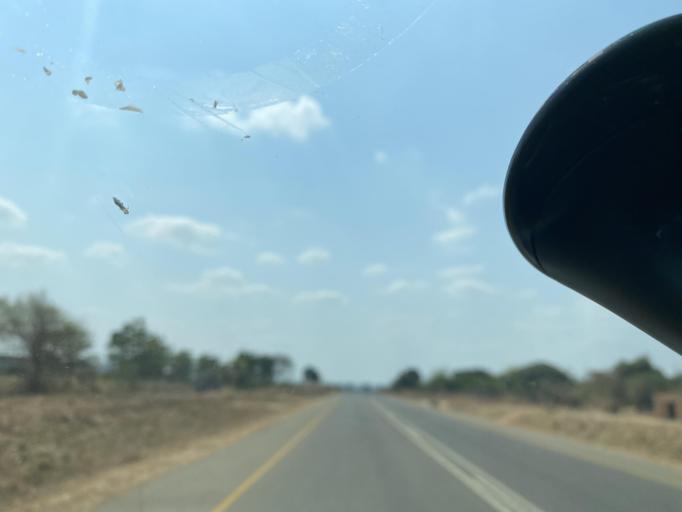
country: ZM
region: Lusaka
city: Chongwe
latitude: -15.5908
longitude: 28.7135
